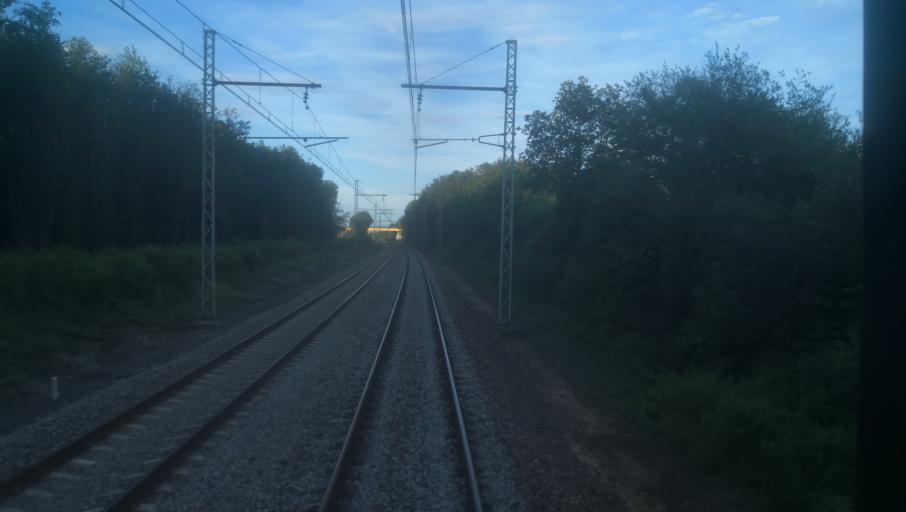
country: FR
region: Centre
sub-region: Departement de l'Indre
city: Saint-Maur
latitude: 46.7731
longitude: 1.6289
